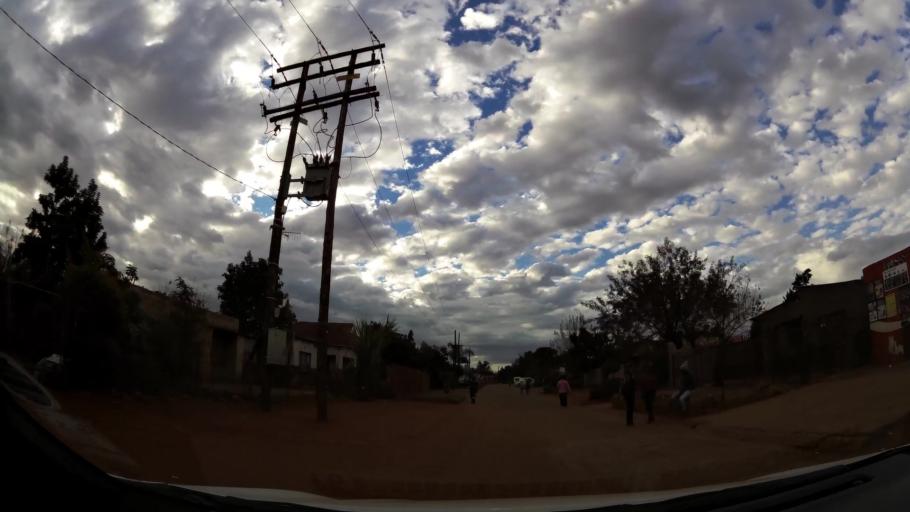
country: ZA
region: Limpopo
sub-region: Waterberg District Municipality
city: Modimolle
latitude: -24.5257
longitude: 28.7229
